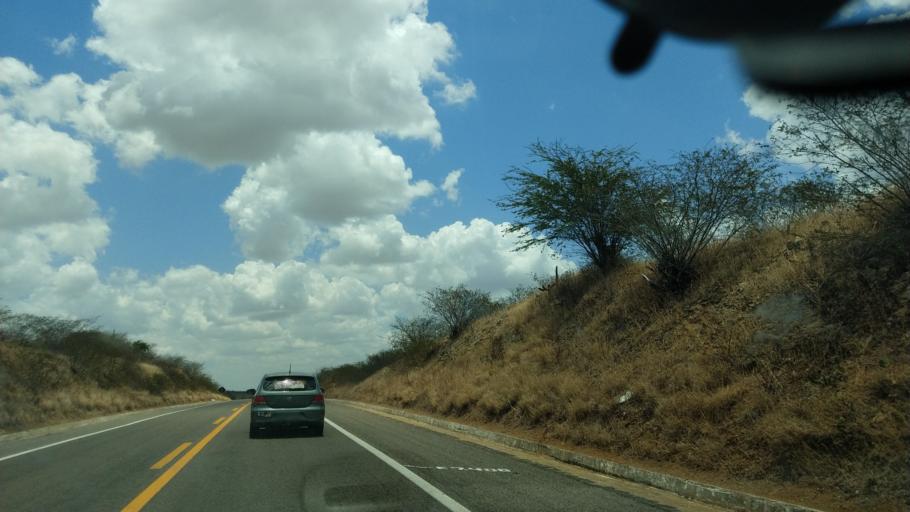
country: BR
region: Rio Grande do Norte
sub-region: Cerro Cora
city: Cerro Cora
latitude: -6.2090
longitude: -36.2918
